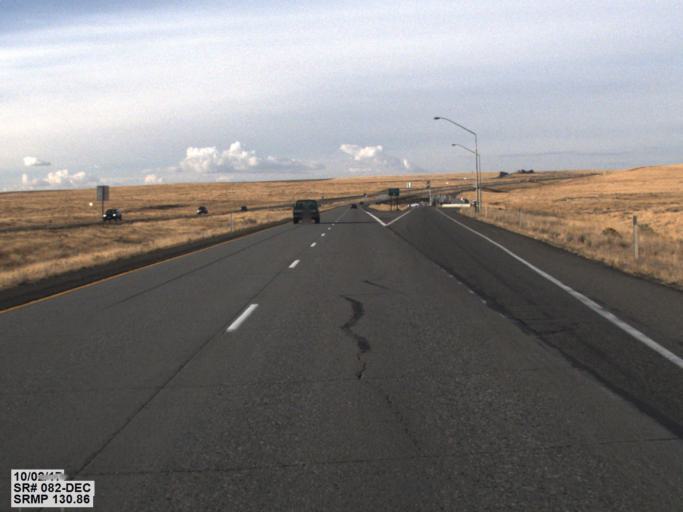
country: US
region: Oregon
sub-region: Umatilla County
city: Umatilla
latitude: 45.9555
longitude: -119.3398
